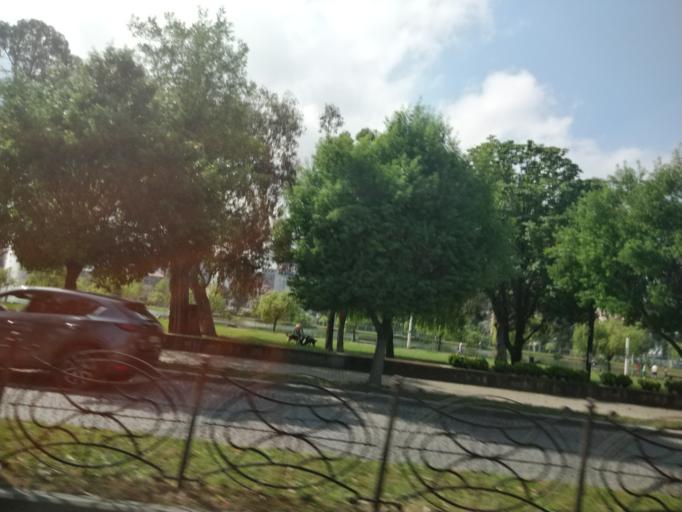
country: GE
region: Ajaria
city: Batumi
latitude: 41.6484
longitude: 41.6246
